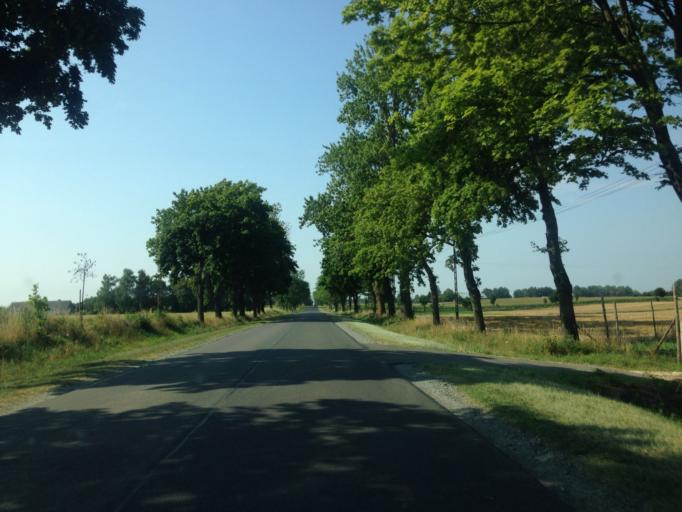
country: PL
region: Kujawsko-Pomorskie
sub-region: Powiat brodnicki
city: Swiedziebnia
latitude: 53.1458
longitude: 19.5453
